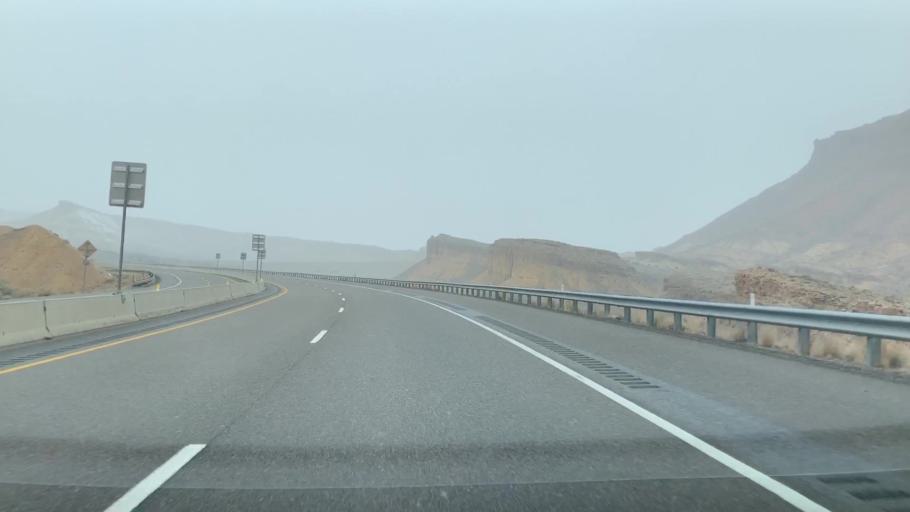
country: US
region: Utah
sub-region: Carbon County
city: East Carbon City
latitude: 38.9268
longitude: -110.4559
